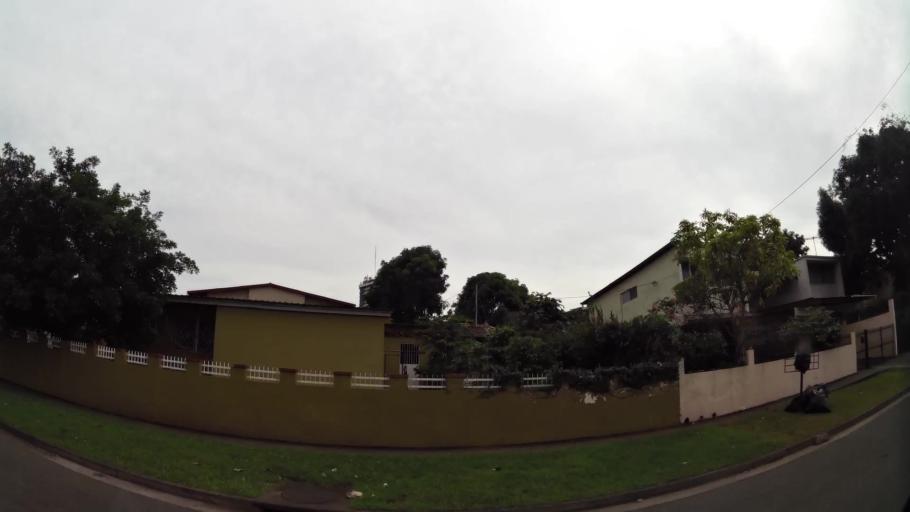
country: PA
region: Panama
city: Panama
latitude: 9.0192
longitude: -79.5217
